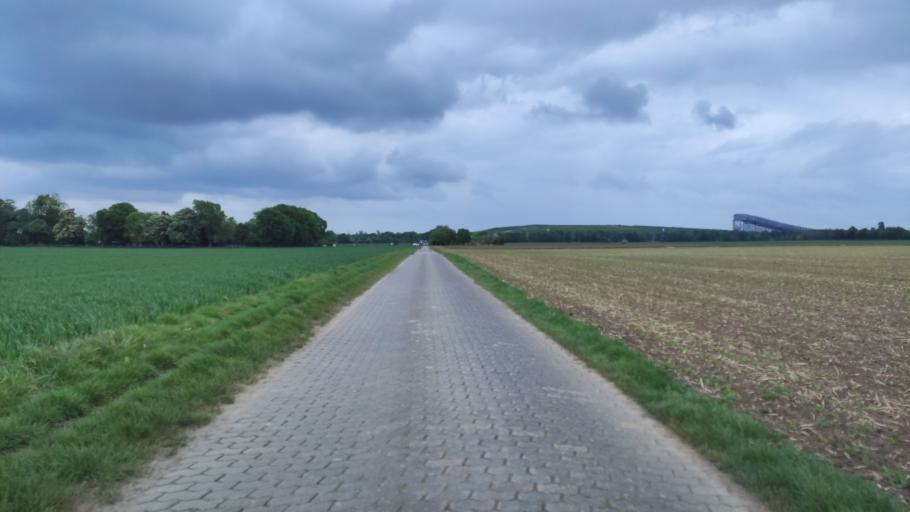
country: DE
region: North Rhine-Westphalia
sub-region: Regierungsbezirk Dusseldorf
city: Neuss
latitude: 51.1879
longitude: 6.6504
